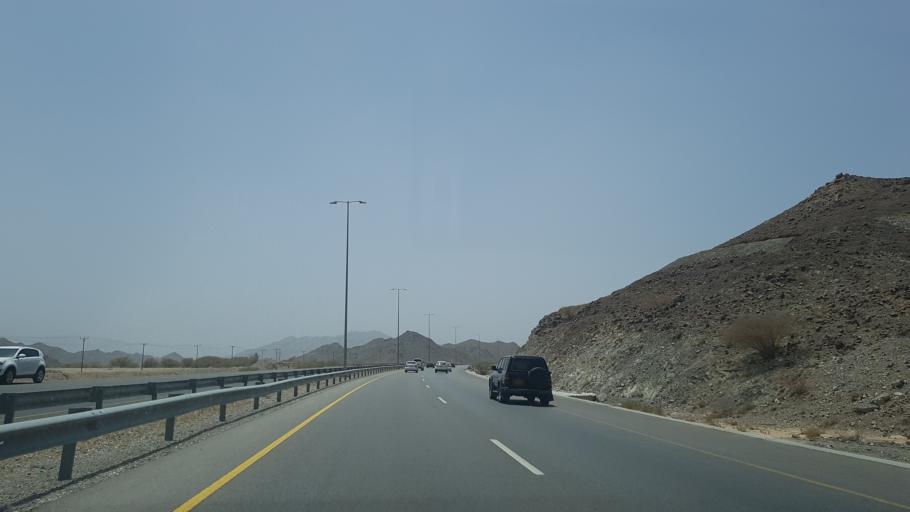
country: OM
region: Muhafazat ad Dakhiliyah
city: Bidbid
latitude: 23.4028
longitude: 58.0787
